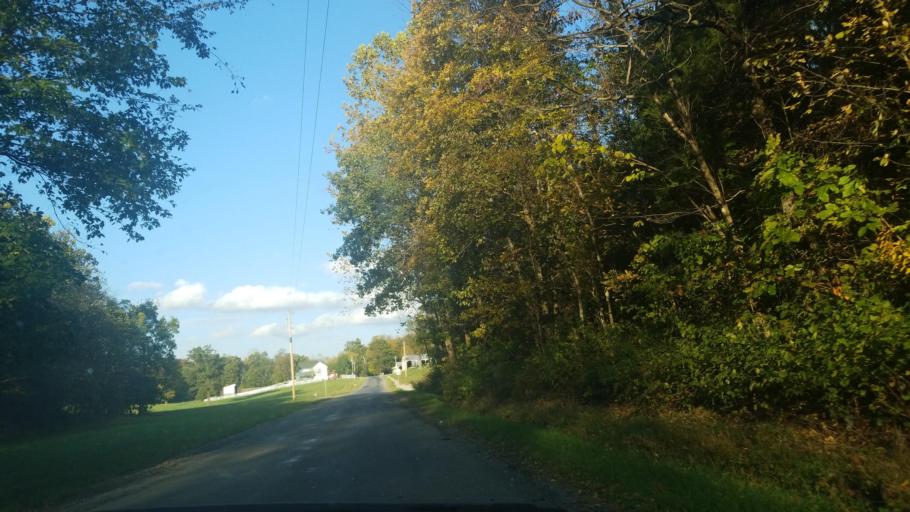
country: US
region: Illinois
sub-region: Williamson County
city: Marion
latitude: 37.7654
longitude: -88.7767
